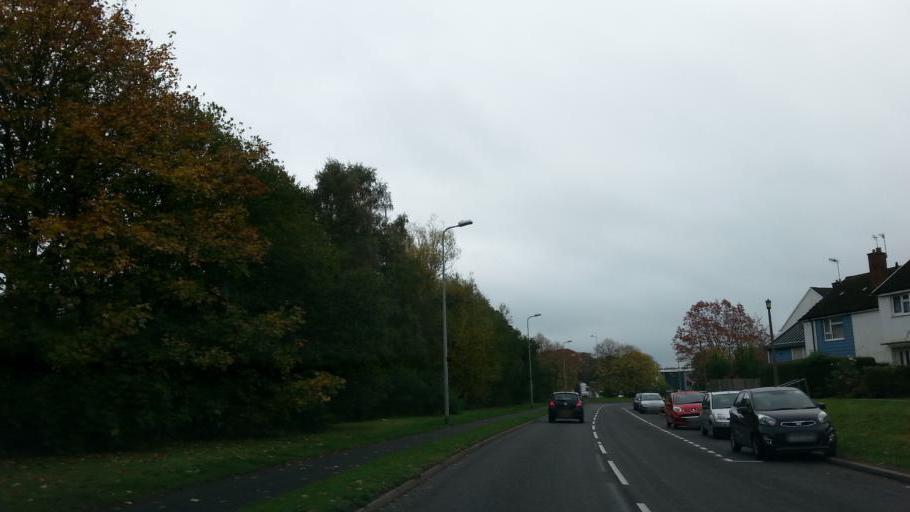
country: GB
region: England
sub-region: Worcestershire
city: Bromsgrove
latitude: 52.3238
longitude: -2.0607
